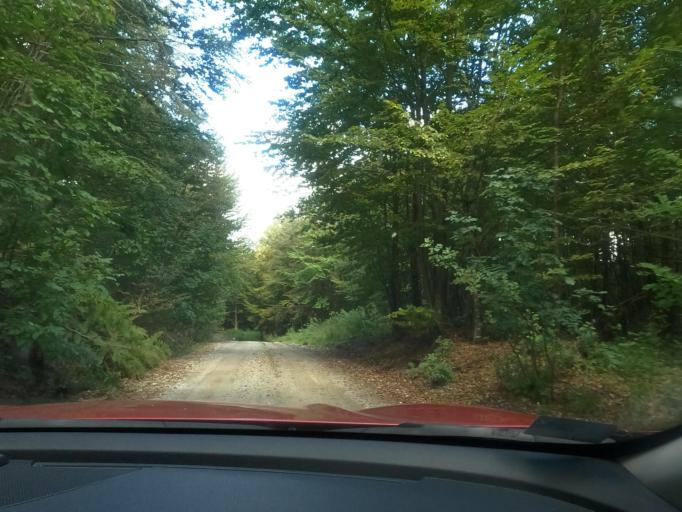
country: BA
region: Federation of Bosnia and Herzegovina
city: Velika Kladusa
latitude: 45.2683
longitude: 15.7781
